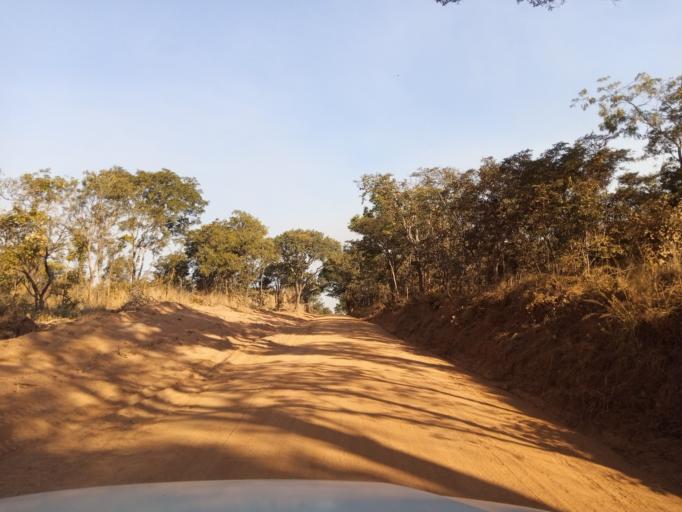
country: CD
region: Katanga
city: Lubumbashi
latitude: -11.3052
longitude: 27.2833
